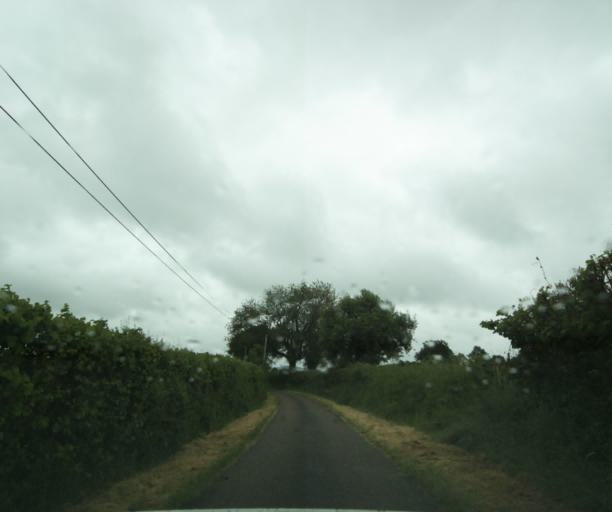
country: FR
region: Bourgogne
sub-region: Departement de Saone-et-Loire
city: Charolles
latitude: 46.4827
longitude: 4.4204
